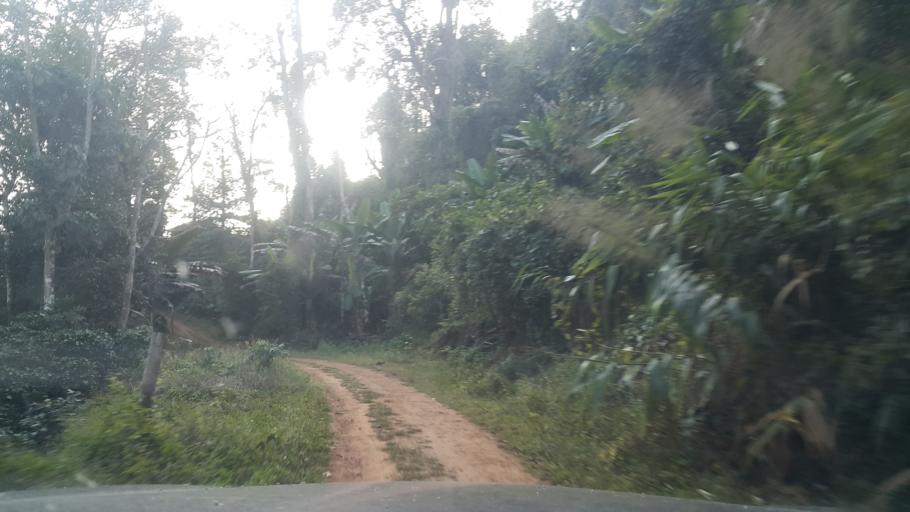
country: TH
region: Chiang Mai
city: Samoeng
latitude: 19.0093
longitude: 98.6478
